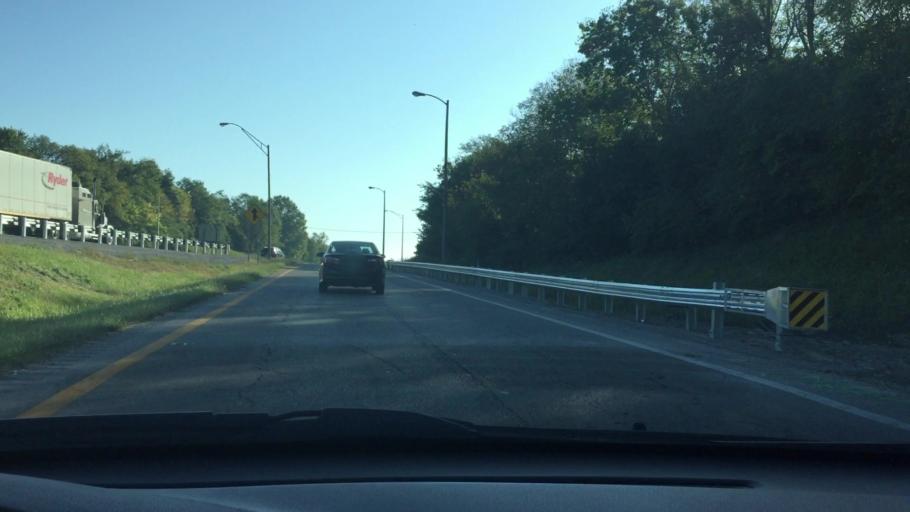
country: US
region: Kentucky
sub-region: Fayette County
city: Lexington
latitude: 37.9909
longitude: -84.4924
